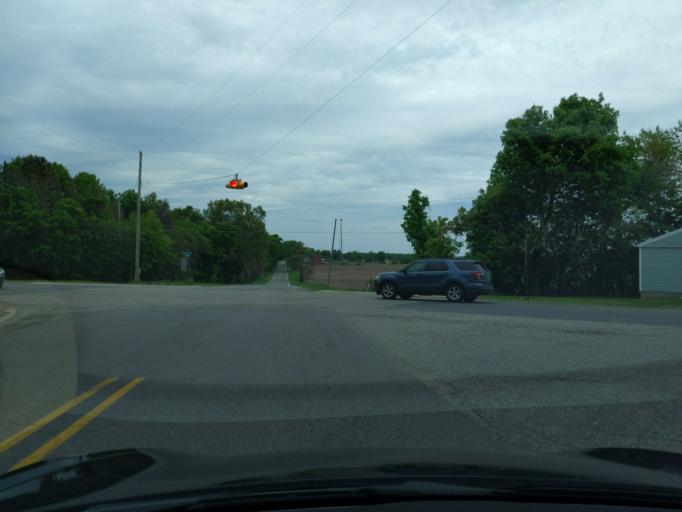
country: US
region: Michigan
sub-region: Ingham County
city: Mason
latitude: 42.5412
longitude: -84.3566
